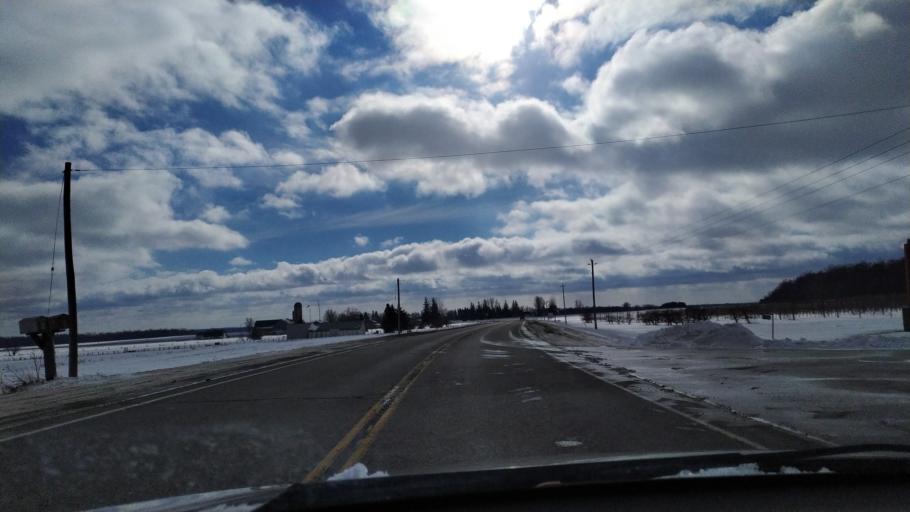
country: CA
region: Ontario
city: Waterloo
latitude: 43.5878
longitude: -80.6081
